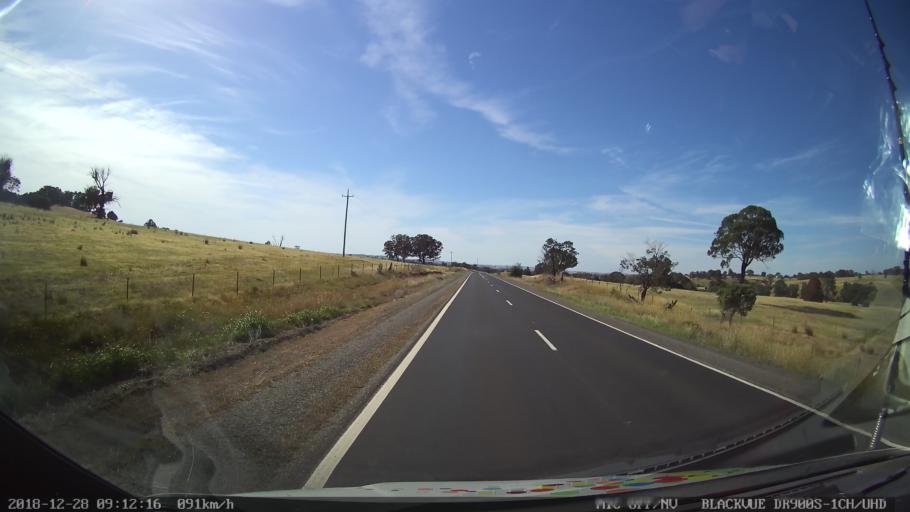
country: AU
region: New South Wales
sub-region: Upper Lachlan Shire
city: Crookwell
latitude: -34.2535
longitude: 149.3404
